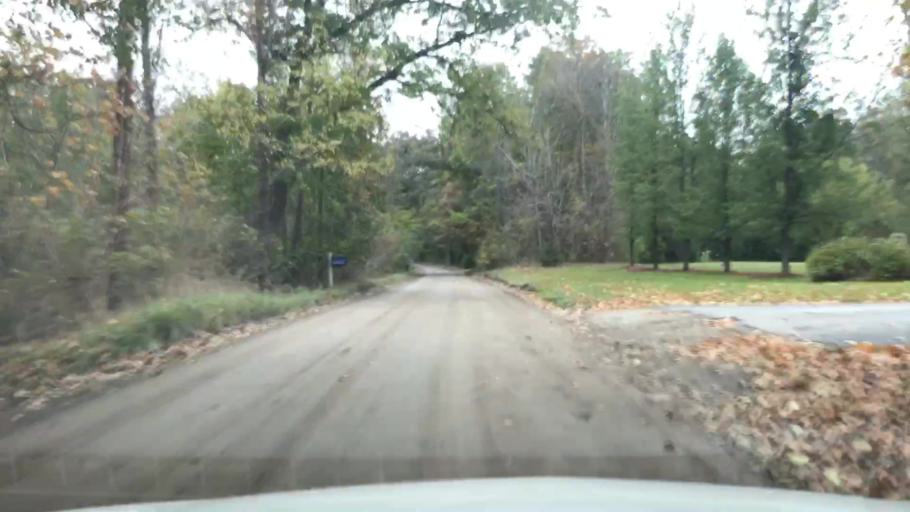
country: US
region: Michigan
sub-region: Oakland County
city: Rochester
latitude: 42.7481
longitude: -83.1011
